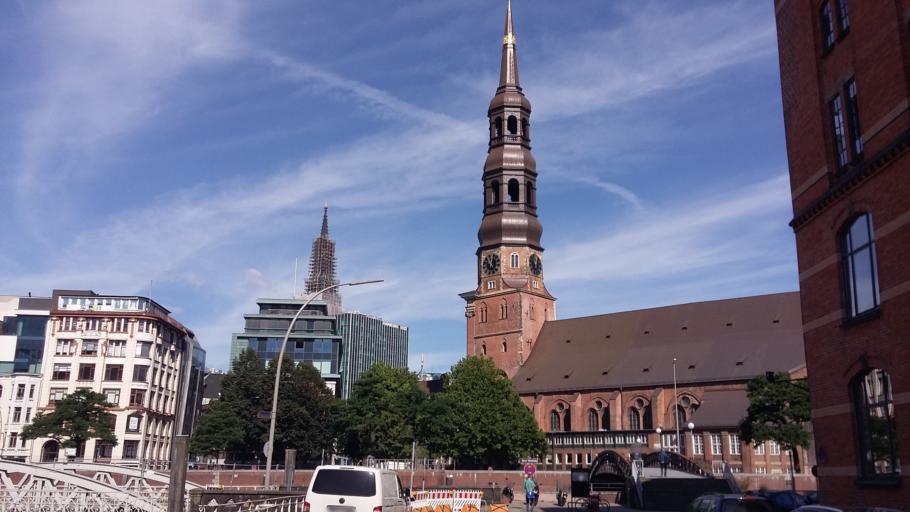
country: DE
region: Hamburg
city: Altstadt
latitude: 53.5446
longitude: 9.9952
